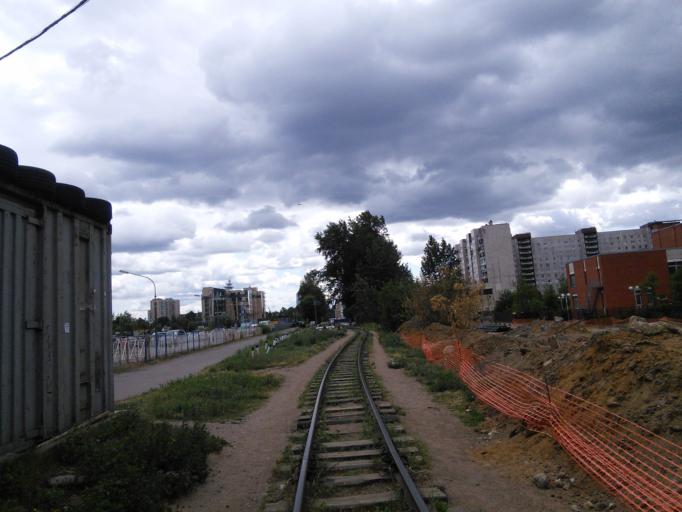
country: RU
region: St.-Petersburg
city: Kolomyagi
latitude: 60.0272
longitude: 30.2945
